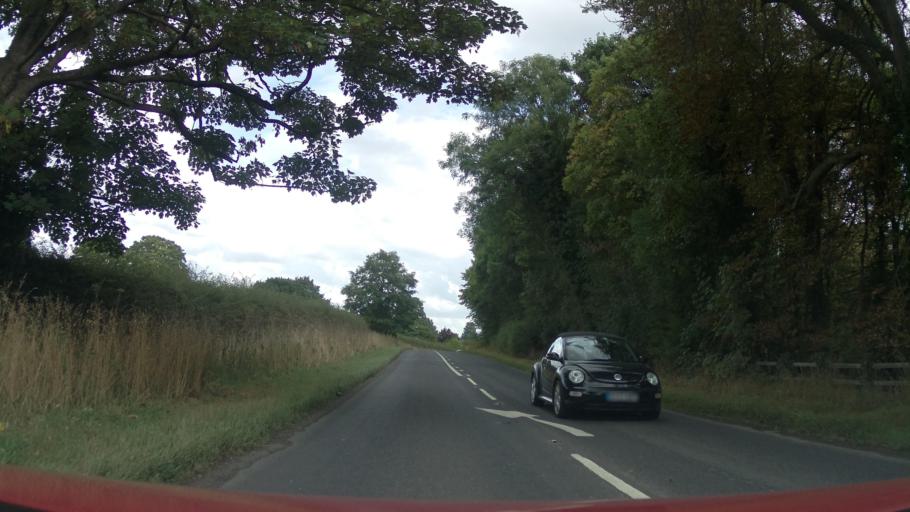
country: GB
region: England
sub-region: North Yorkshire
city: Ripon
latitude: 54.1538
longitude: -1.5363
